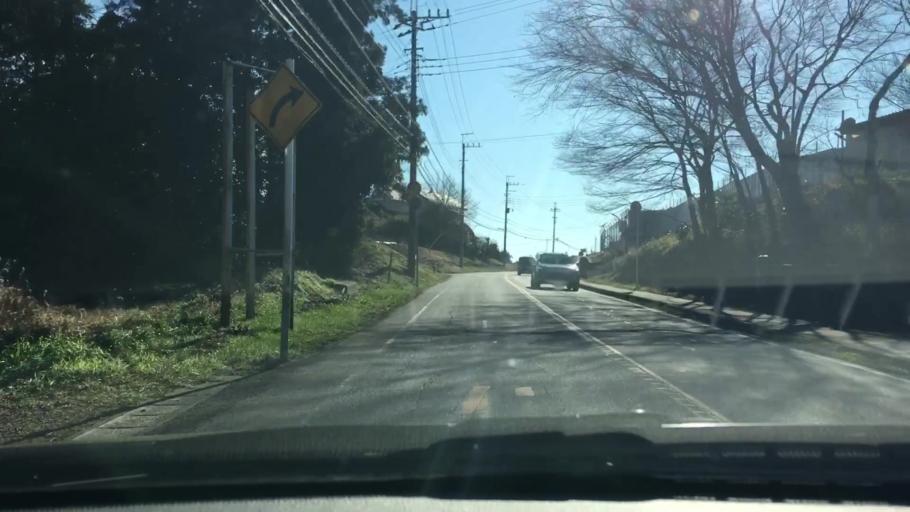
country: JP
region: Chiba
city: Shisui
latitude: 35.7099
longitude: 140.3163
